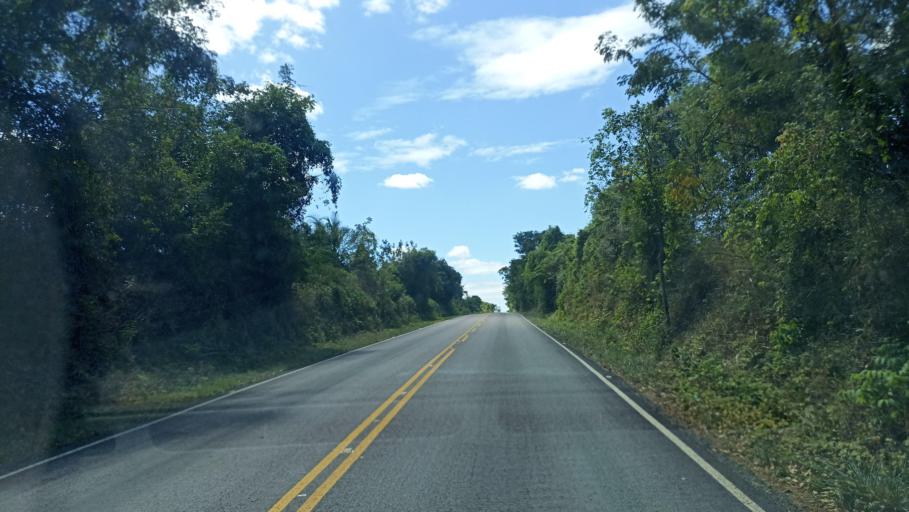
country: BR
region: Bahia
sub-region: Andarai
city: Vera Cruz
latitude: -12.7508
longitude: -41.3276
